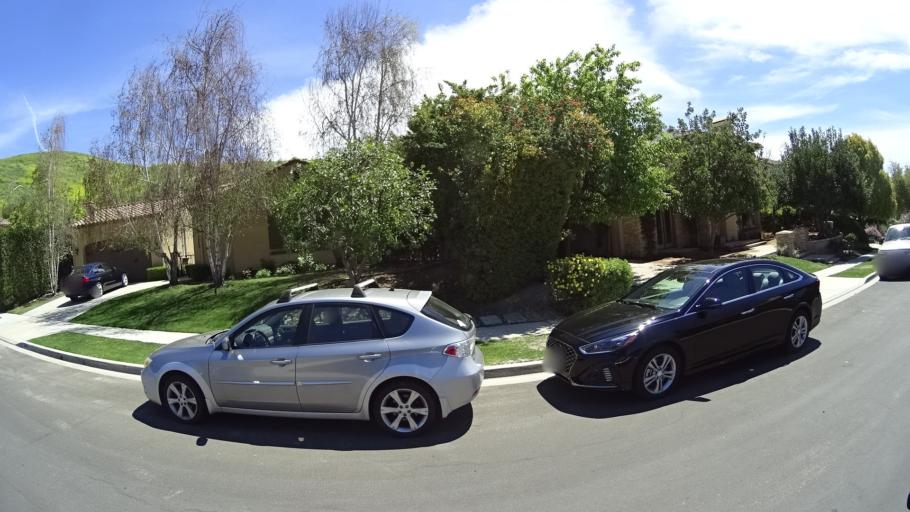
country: US
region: California
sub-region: Ventura County
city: Thousand Oaks
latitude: 34.1832
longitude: -118.8389
